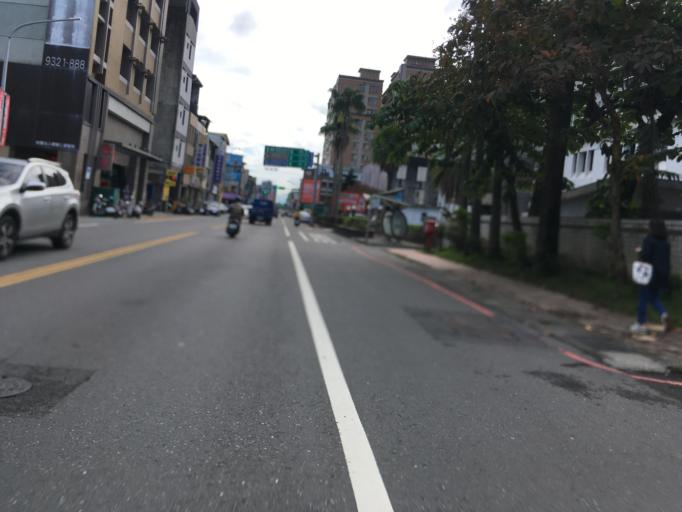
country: TW
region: Taiwan
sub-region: Yilan
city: Yilan
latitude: 24.7490
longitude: 121.7542
